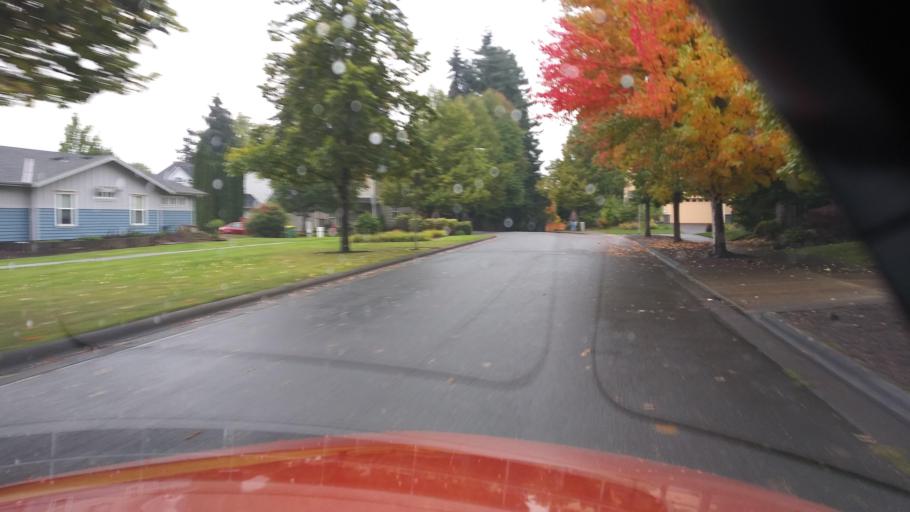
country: US
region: Oregon
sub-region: Washington County
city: Forest Grove
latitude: 45.5351
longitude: -123.1273
